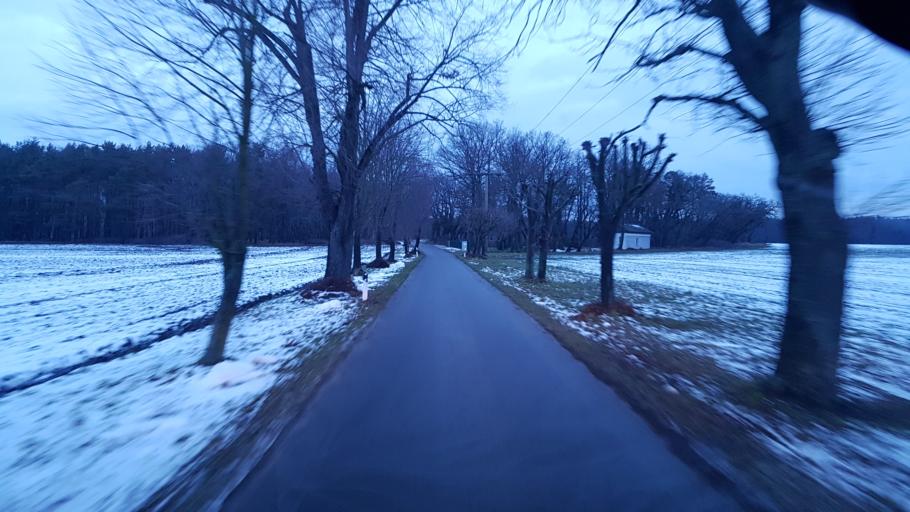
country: DE
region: Brandenburg
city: Neupetershain
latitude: 51.6082
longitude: 14.1284
